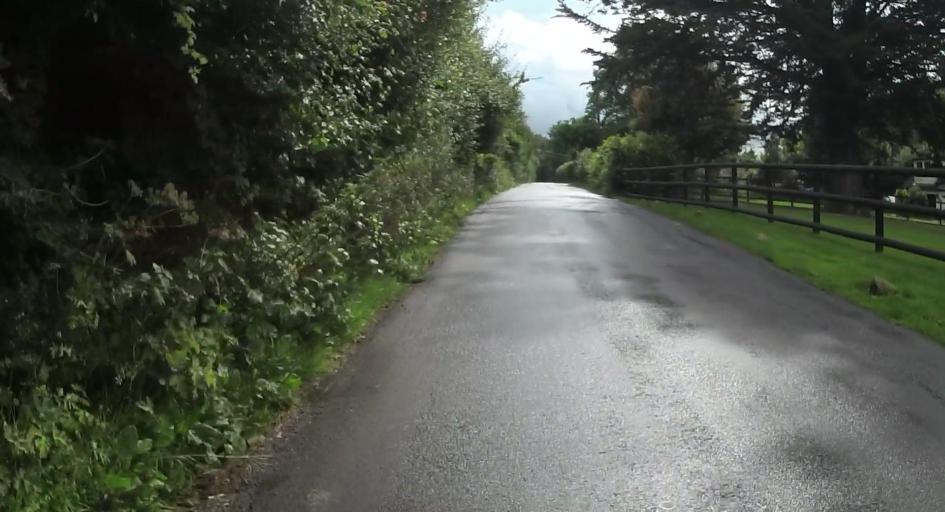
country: GB
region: England
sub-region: Hampshire
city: Andover
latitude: 51.2208
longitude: -1.4344
